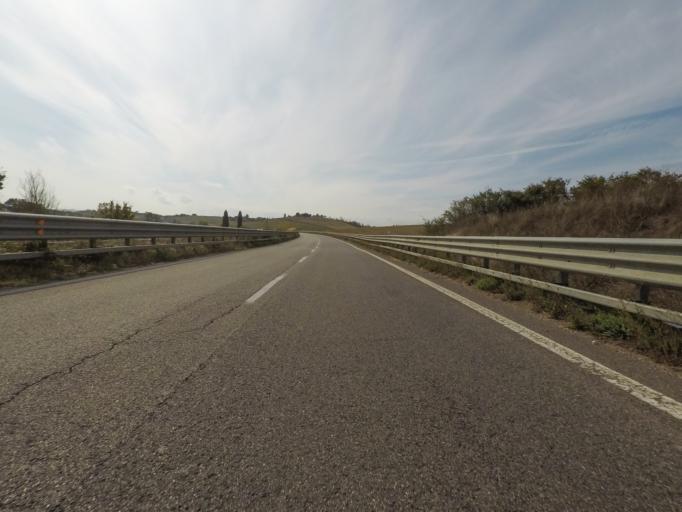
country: IT
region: Tuscany
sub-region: Provincia di Siena
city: Siena
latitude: 43.2865
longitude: 11.3331
